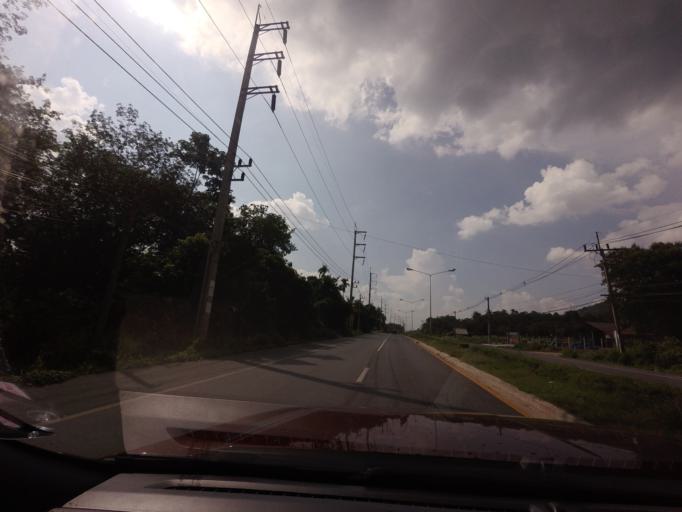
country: TH
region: Yala
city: Yala
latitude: 6.4778
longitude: 101.2655
